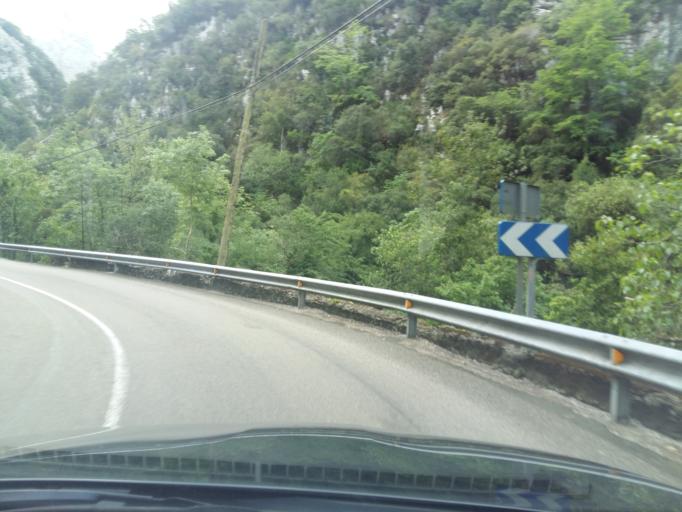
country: ES
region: Cantabria
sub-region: Provincia de Cantabria
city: Tresviso
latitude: 43.3104
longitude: -4.6092
